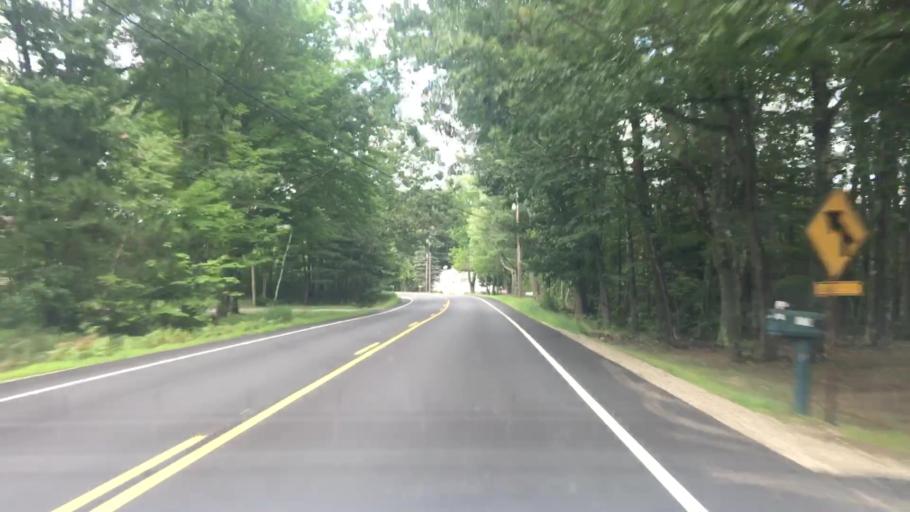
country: US
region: Maine
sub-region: York County
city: West Kennebunk
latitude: 43.4679
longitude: -70.6022
